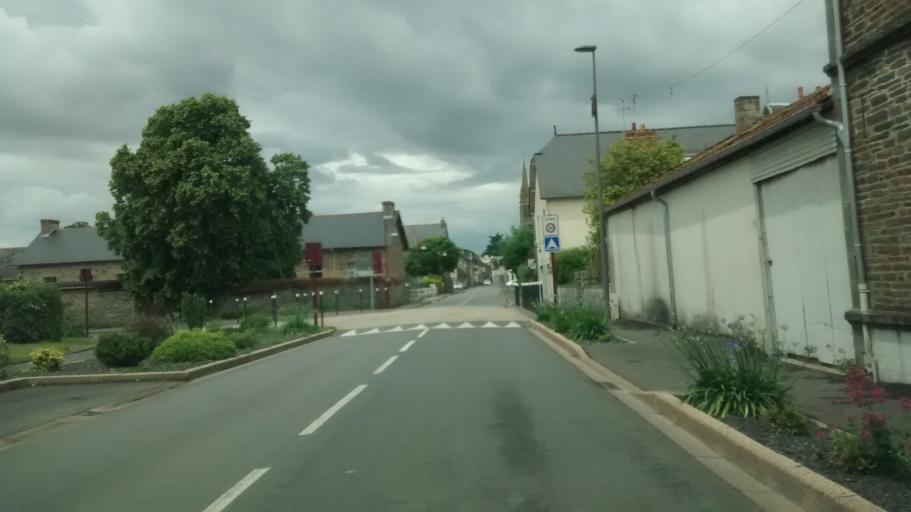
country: FR
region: Brittany
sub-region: Departement du Morbihan
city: Carentoir
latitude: 47.8140
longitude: -2.1313
